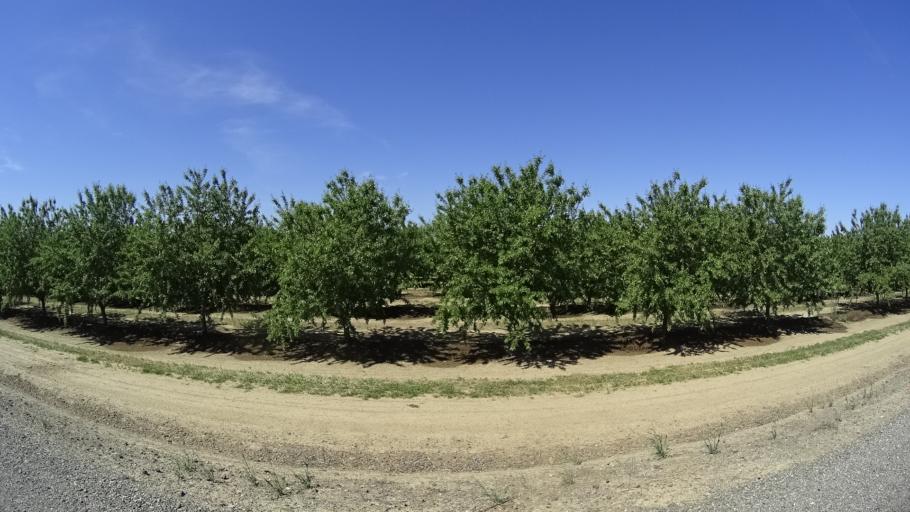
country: US
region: California
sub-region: Glenn County
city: Willows
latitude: 39.6323
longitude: -122.1413
